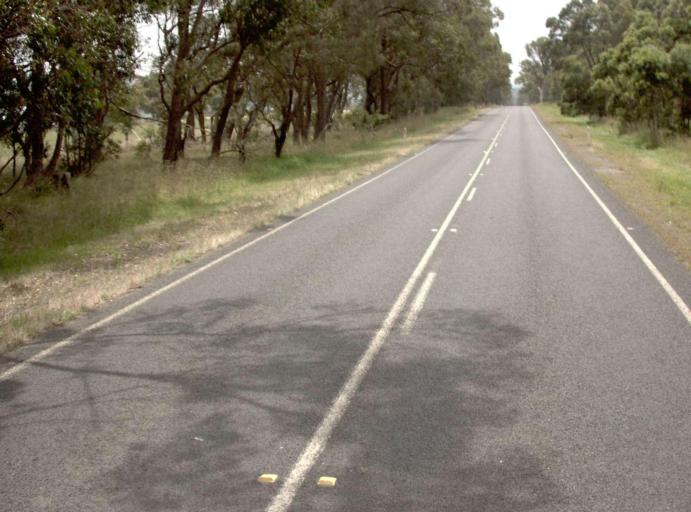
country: AU
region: Victoria
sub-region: Latrobe
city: Traralgon
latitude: -38.4831
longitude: 146.7149
